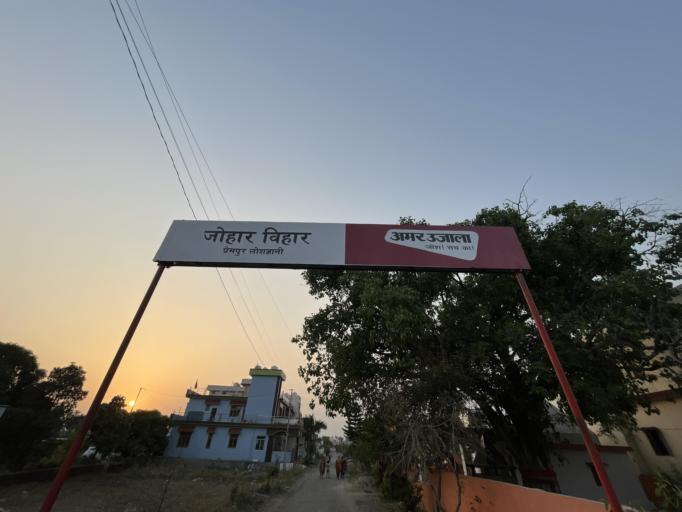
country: IN
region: Uttarakhand
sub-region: Naini Tal
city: Haldwani
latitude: 29.1913
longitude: 79.4800
